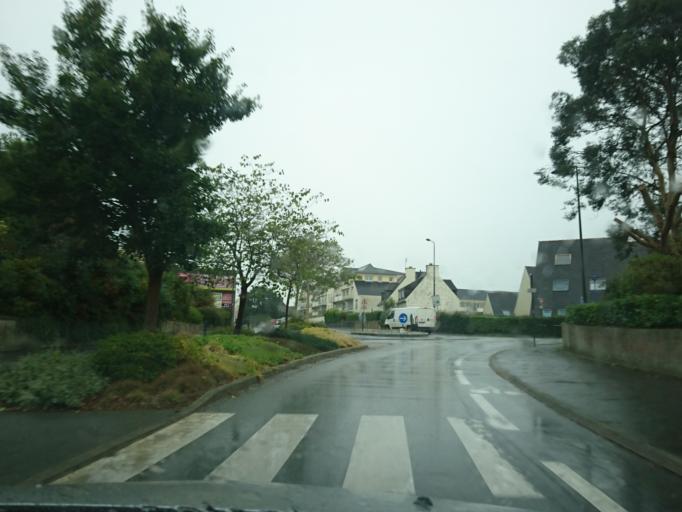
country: FR
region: Brittany
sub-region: Departement du Finistere
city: Plabennec
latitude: 48.4976
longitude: -4.4279
